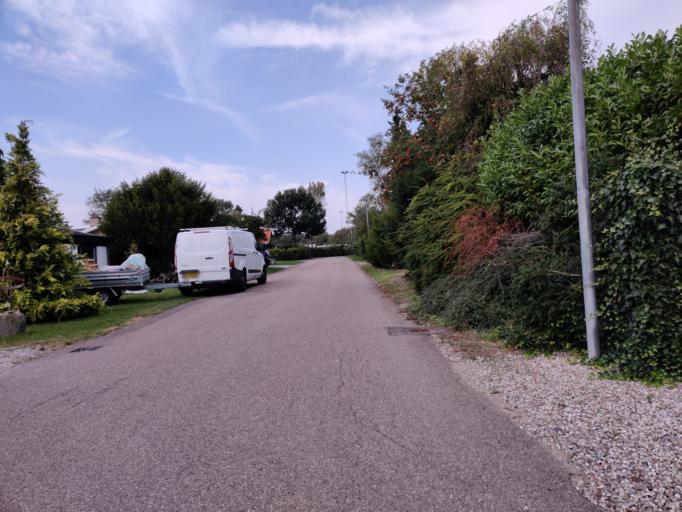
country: DK
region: Zealand
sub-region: Guldborgsund Kommune
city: Nykobing Falster
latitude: 54.7066
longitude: 11.9206
